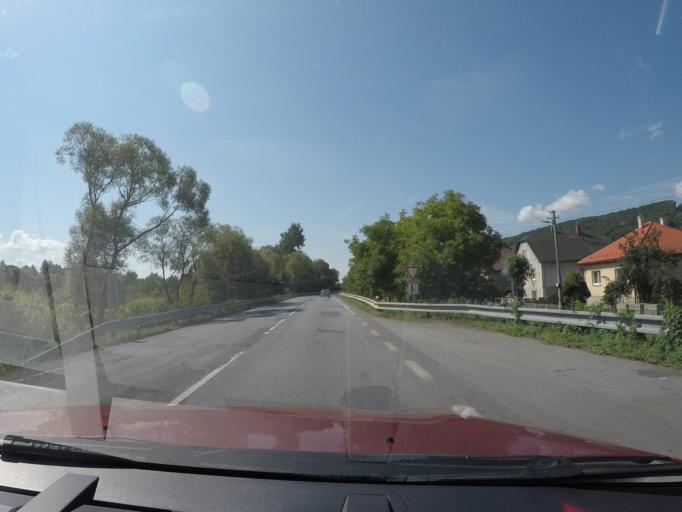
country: SK
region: Presovsky
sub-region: Okres Presov
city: Presov
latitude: 48.9527
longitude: 21.2415
